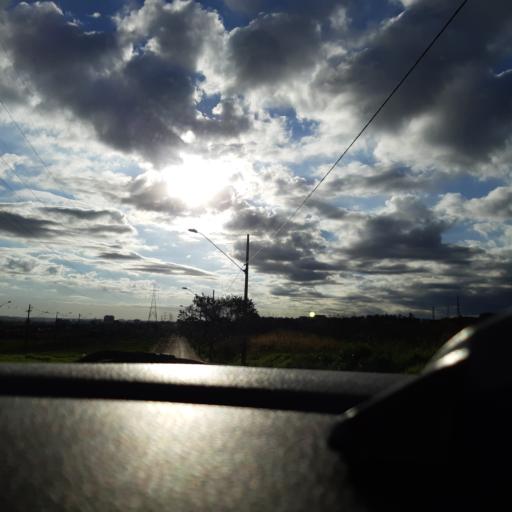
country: BR
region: Sao Paulo
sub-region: Ourinhos
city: Ourinhos
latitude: -23.0024
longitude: -49.8394
